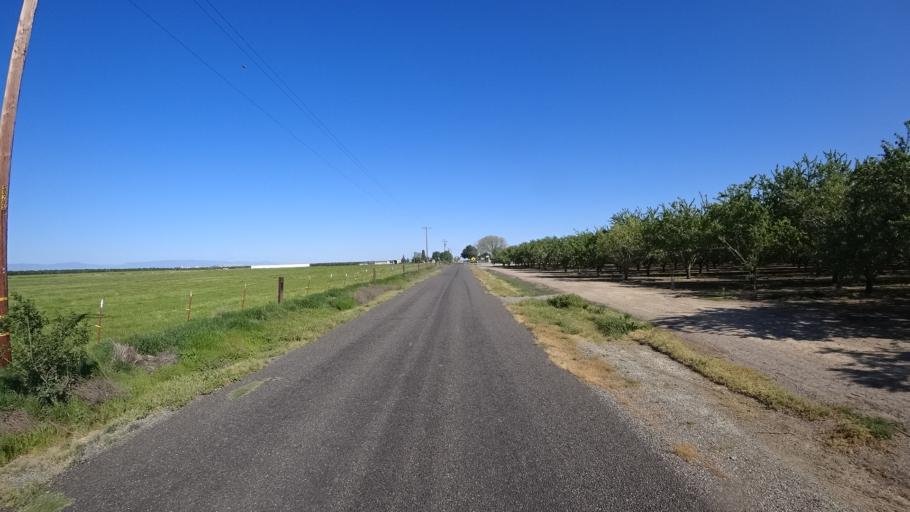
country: US
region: California
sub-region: Glenn County
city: Hamilton City
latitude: 39.7072
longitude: -122.0770
